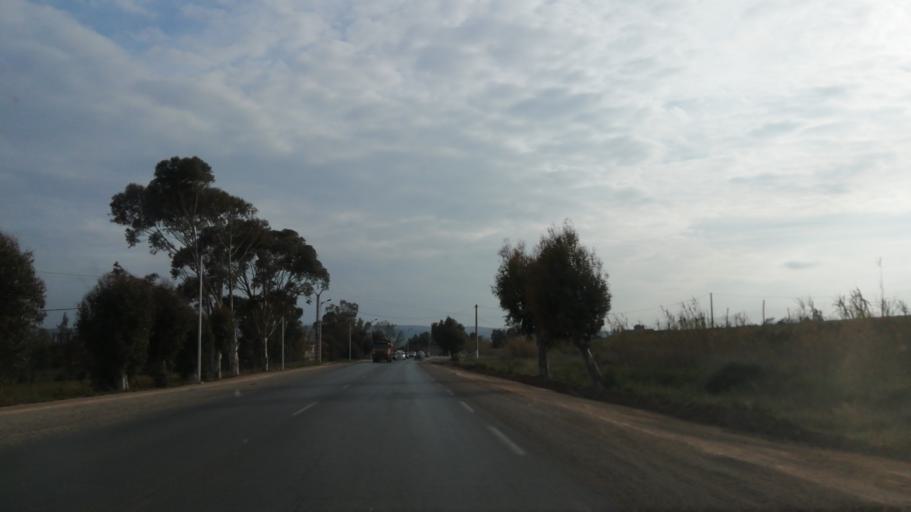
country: DZ
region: Mostaganem
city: Mostaganem
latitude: 35.8809
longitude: 0.0785
